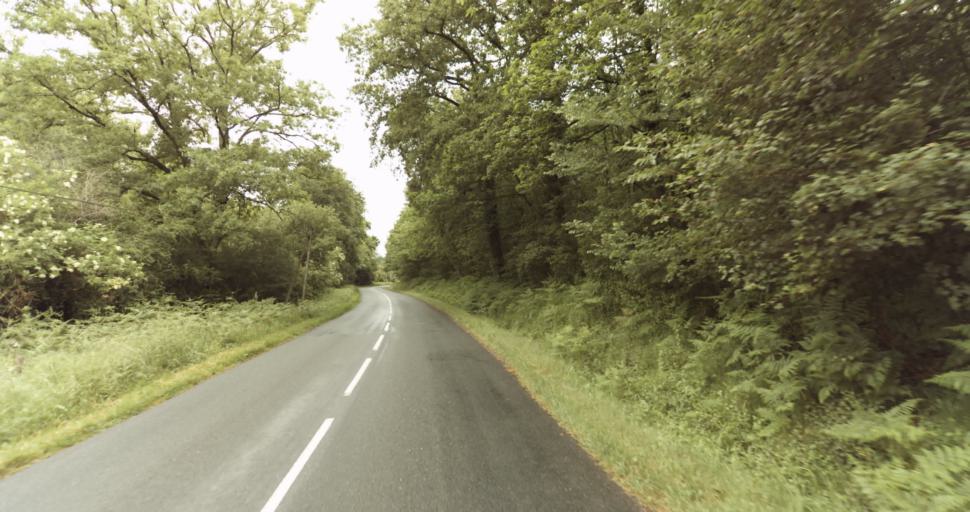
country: FR
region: Aquitaine
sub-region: Departement de la Dordogne
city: Belves
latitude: 44.7129
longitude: 0.9342
